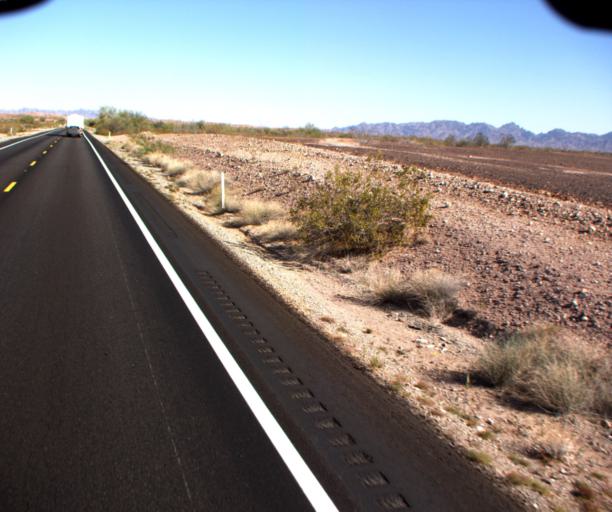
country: US
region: Arizona
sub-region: Yuma County
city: Wellton
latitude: 33.0651
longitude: -114.2933
